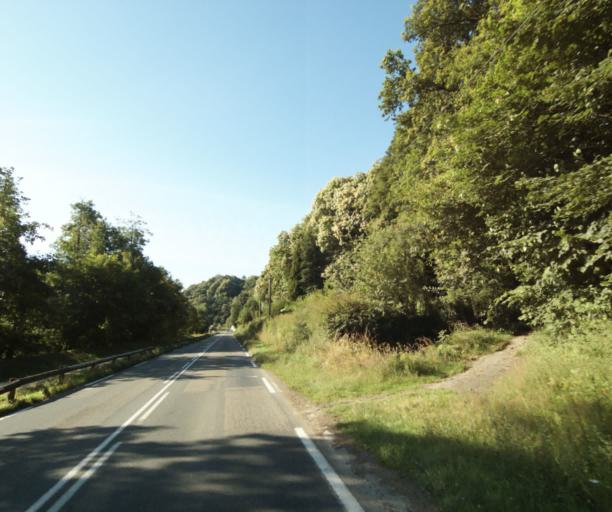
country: FR
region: Pays de la Loire
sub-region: Departement de la Mayenne
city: Laval
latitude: 48.0412
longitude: -0.7650
